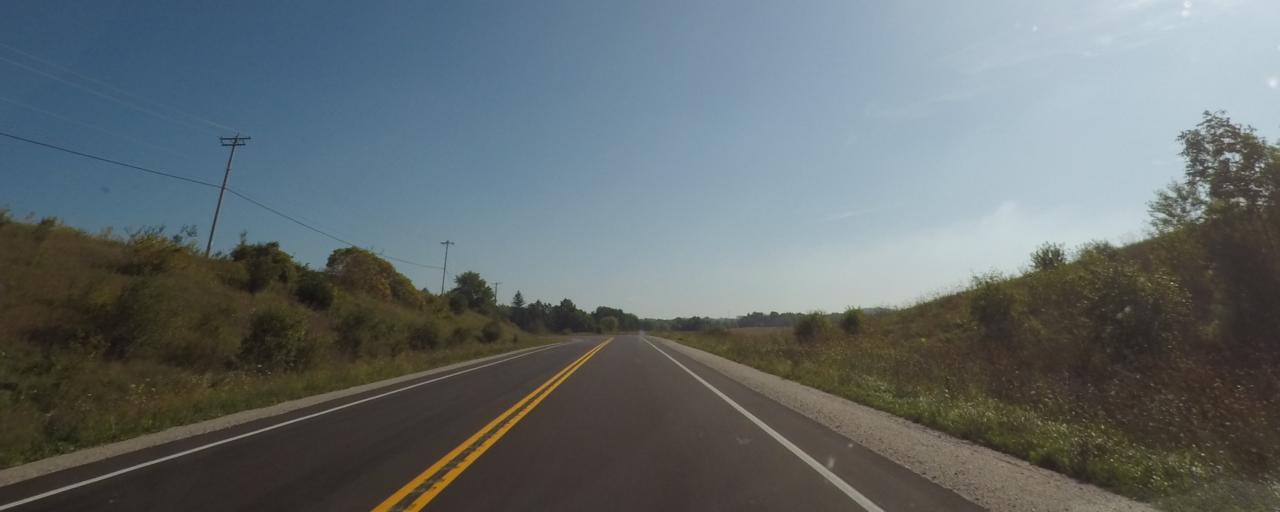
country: US
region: Wisconsin
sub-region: Jefferson County
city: Jefferson
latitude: 43.0099
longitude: -88.7669
